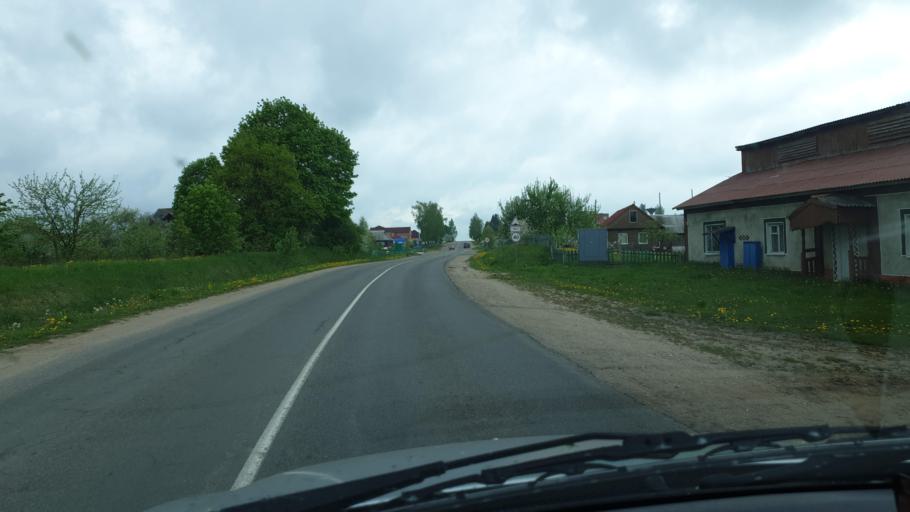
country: BY
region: Vitebsk
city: Lyepyel'
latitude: 54.8868
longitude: 28.6278
